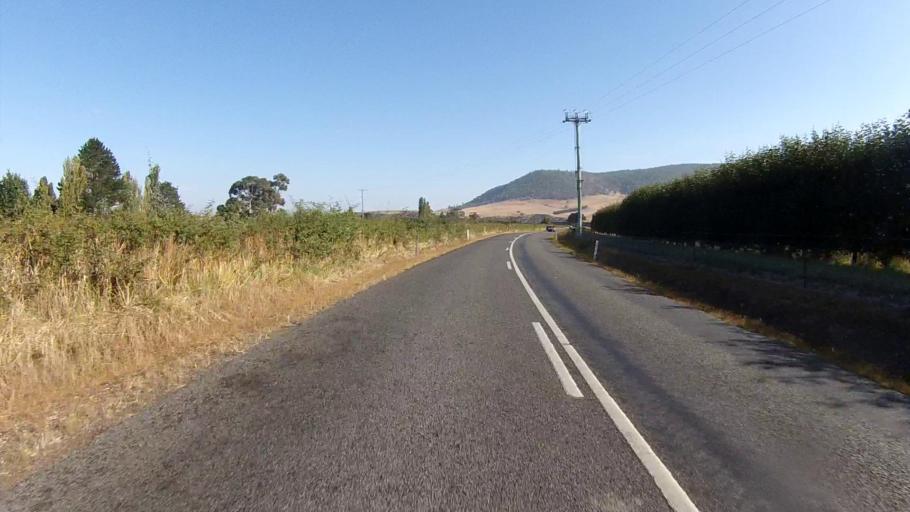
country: AU
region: Tasmania
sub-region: Derwent Valley
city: New Norfolk
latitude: -42.7479
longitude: 146.9727
